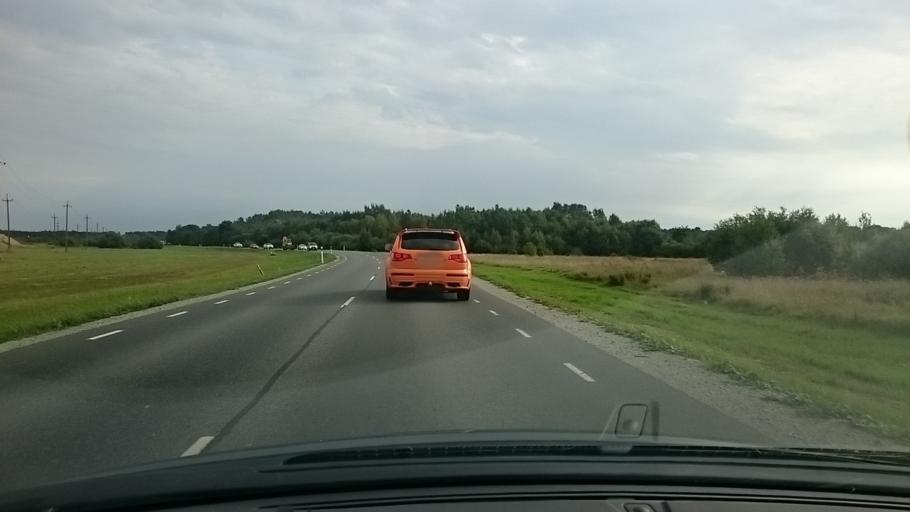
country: EE
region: Harju
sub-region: Harku vald
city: Tabasalu
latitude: 59.4019
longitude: 24.5481
